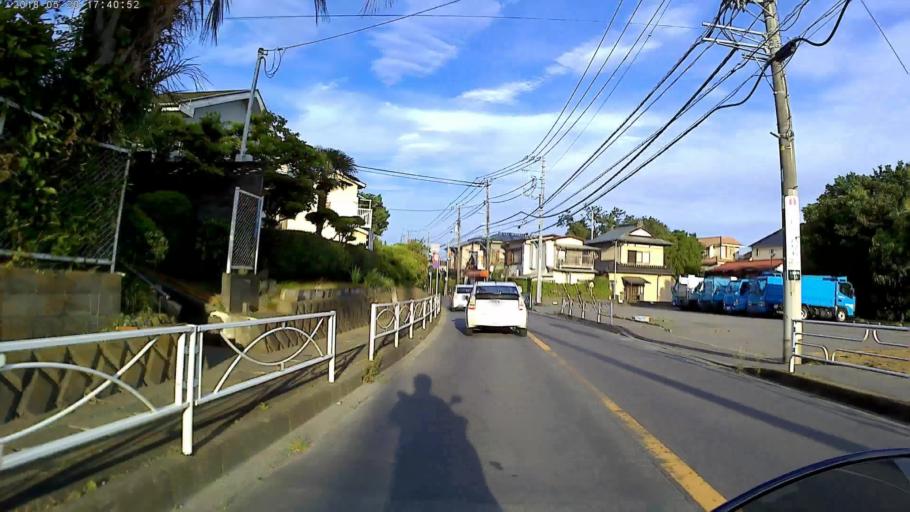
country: JP
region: Kanagawa
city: Ninomiya
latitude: 35.3098
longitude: 139.2738
